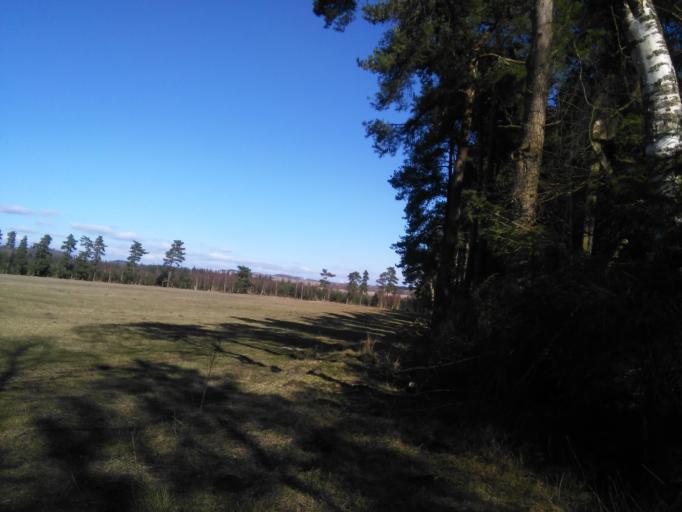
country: DK
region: Central Jutland
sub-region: Skanderborg Kommune
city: Ry
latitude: 56.1004
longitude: 9.7113
